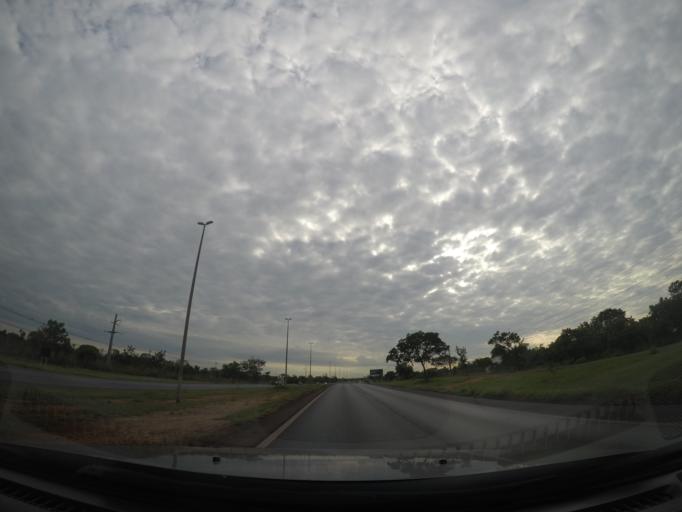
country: BR
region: Goias
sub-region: Planaltina
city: Planaltina
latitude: -15.5946
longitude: -47.6629
